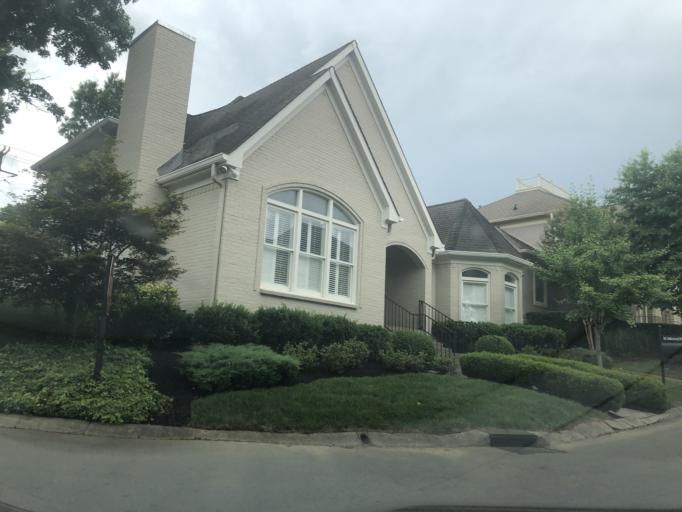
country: US
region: Tennessee
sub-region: Davidson County
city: Forest Hills
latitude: 36.0914
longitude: -86.8200
